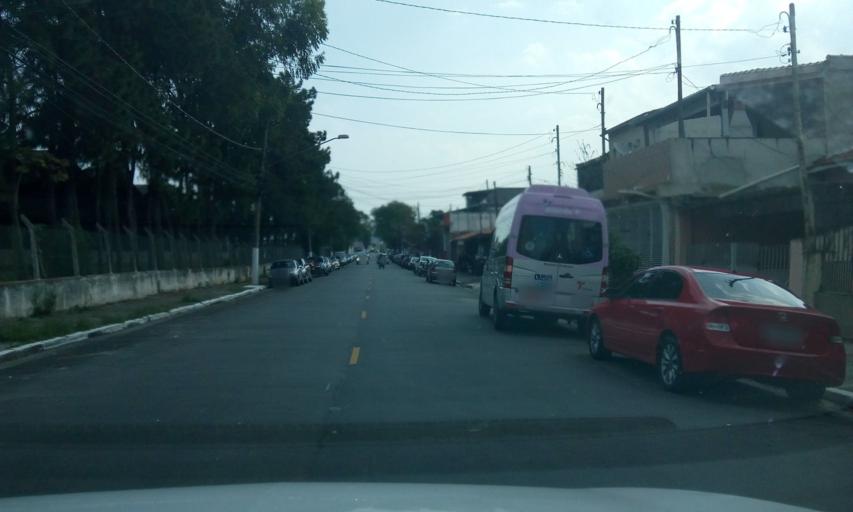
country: BR
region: Sao Paulo
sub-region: Osasco
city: Osasco
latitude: -23.5298
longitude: -46.7337
